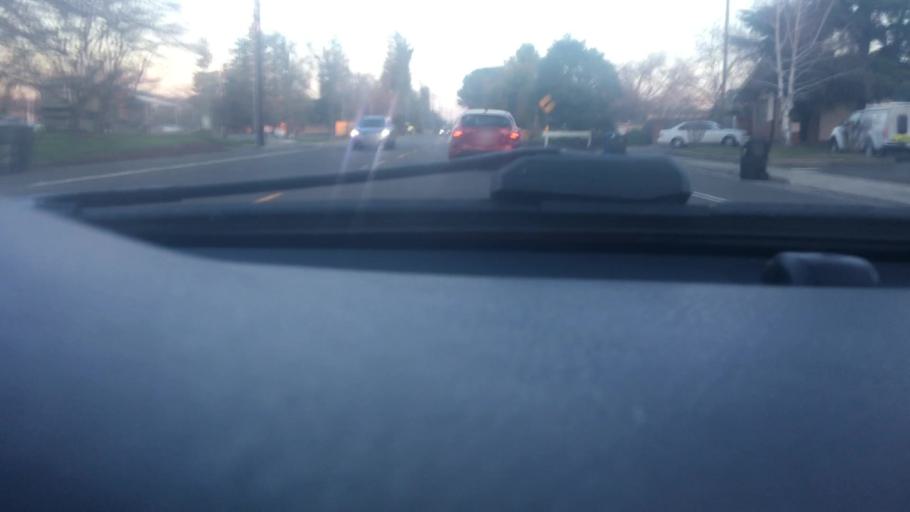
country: US
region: California
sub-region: Sacramento County
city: Carmichael
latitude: 38.6389
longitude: -121.3344
